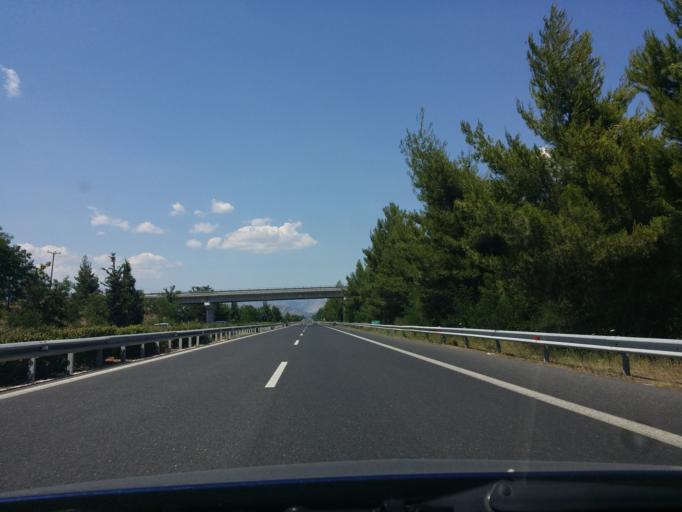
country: GR
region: Peloponnese
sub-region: Nomos Arkadias
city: Tripoli
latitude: 37.5167
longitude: 22.4059
